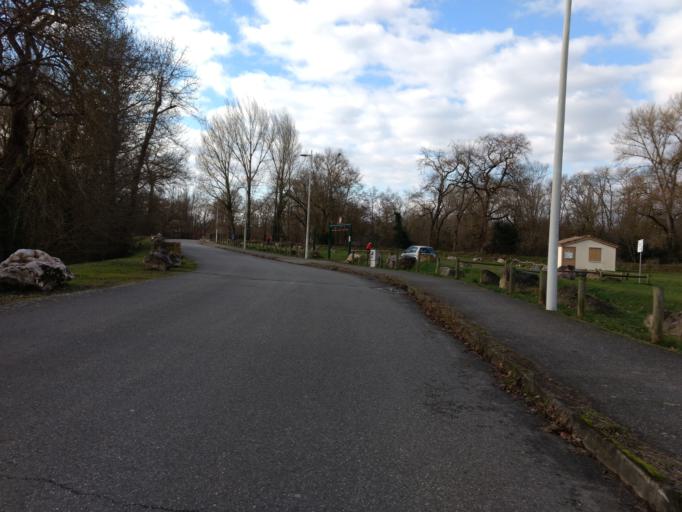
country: FR
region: Midi-Pyrenees
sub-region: Departement de la Haute-Garonne
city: Tournefeuille
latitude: 43.5828
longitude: 1.3517
